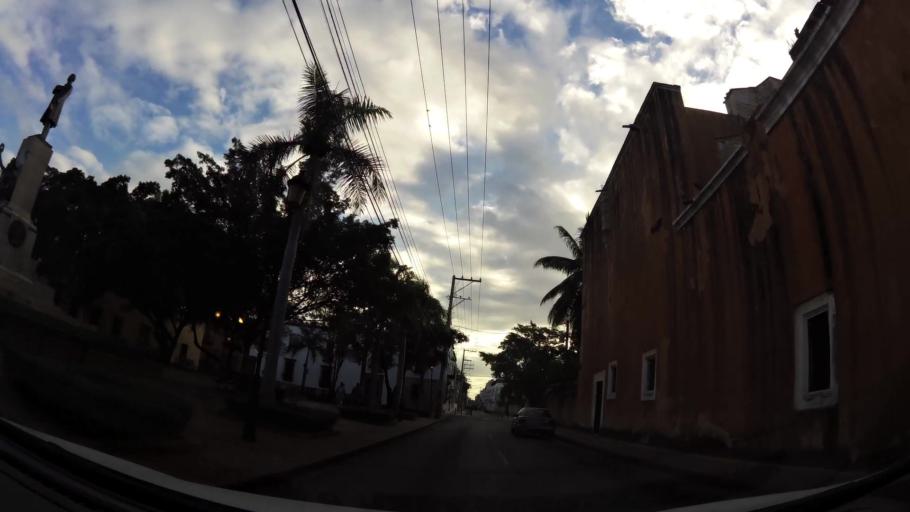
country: DO
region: Nacional
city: Ciudad Nueva
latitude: 18.4715
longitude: -69.8853
